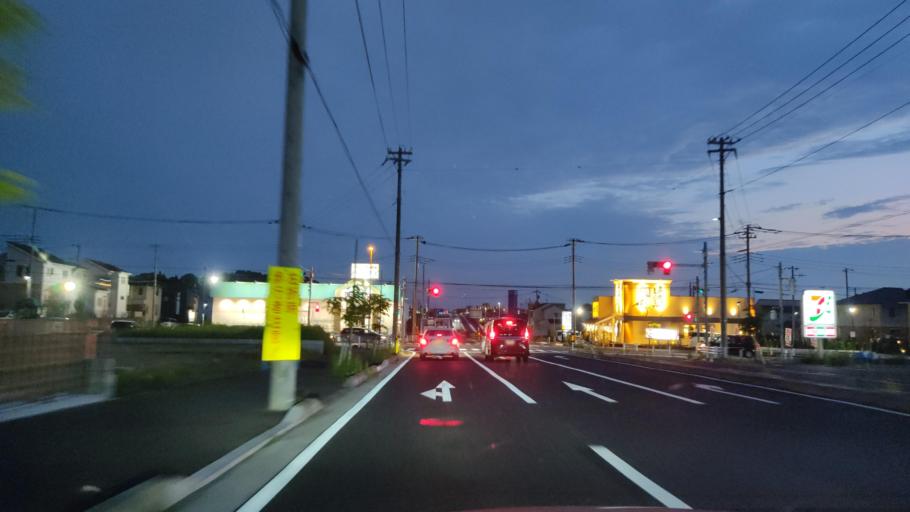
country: JP
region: Chiba
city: Nagareyama
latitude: 35.8481
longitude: 139.9091
